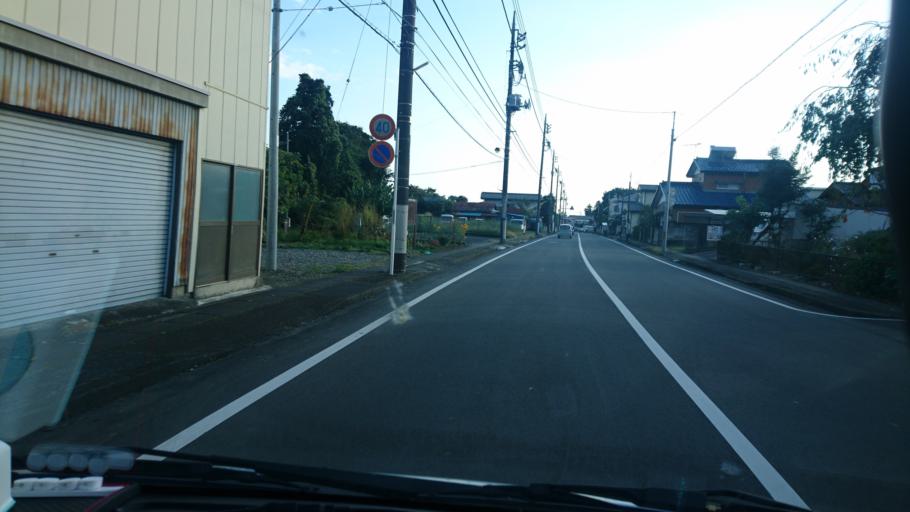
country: JP
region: Gunma
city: Omamacho-omama
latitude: 36.4397
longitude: 139.2775
